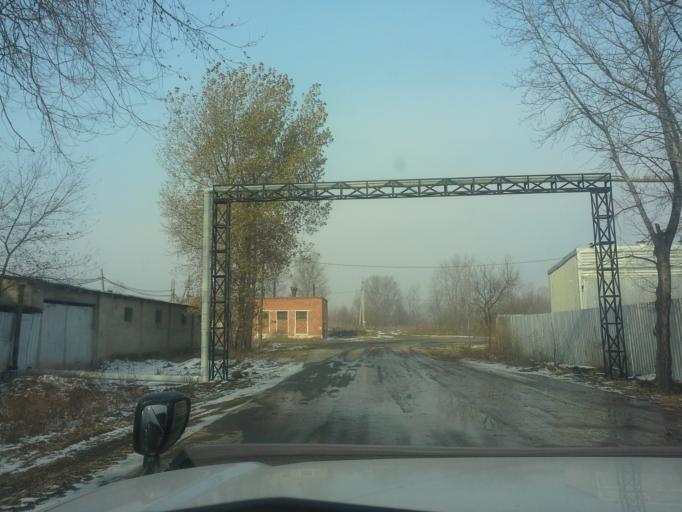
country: RU
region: Jewish Autonomous Oblast
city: Priamurskiy
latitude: 48.5350
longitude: 134.9028
